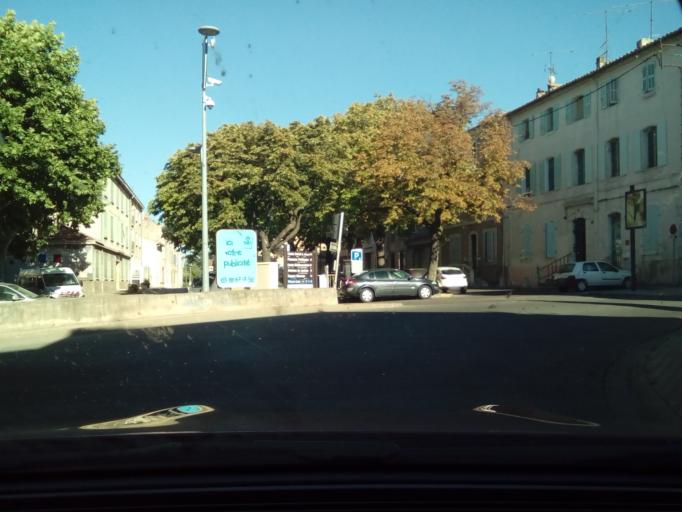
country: FR
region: Provence-Alpes-Cote d'Azur
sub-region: Departement du Var
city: Saint-Maximin-la-Sainte-Baume
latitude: 43.4514
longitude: 5.8619
